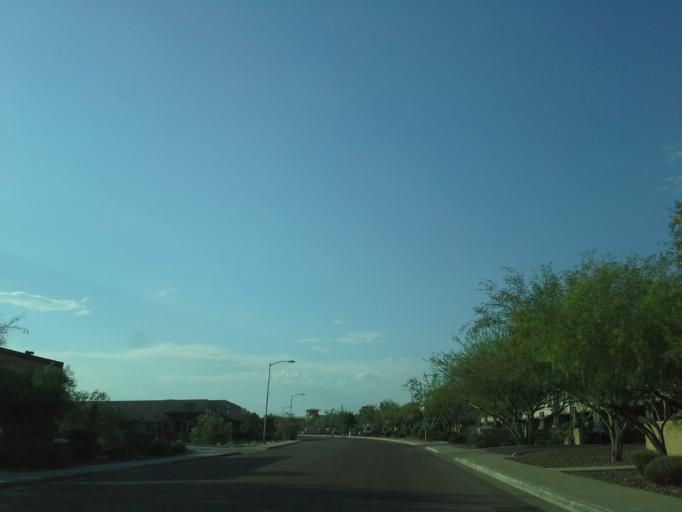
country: US
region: Arizona
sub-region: Maricopa County
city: Anthem
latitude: 33.8653
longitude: -112.1475
